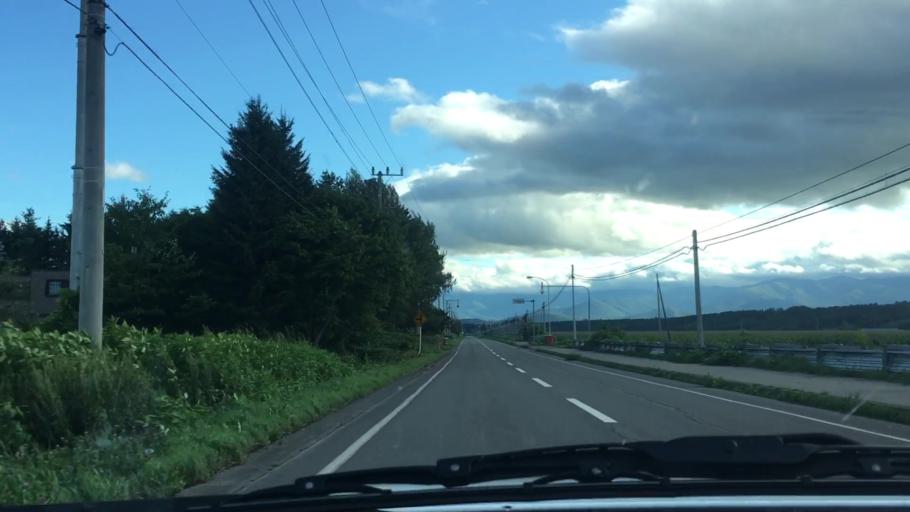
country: JP
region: Hokkaido
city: Otofuke
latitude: 43.1449
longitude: 142.8976
